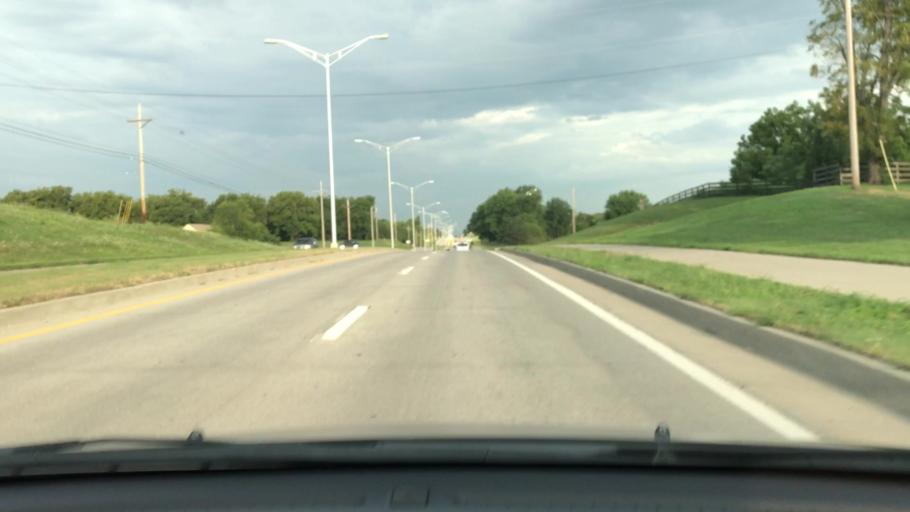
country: US
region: Missouri
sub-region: Cass County
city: Raymore
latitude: 38.8540
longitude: -94.4225
